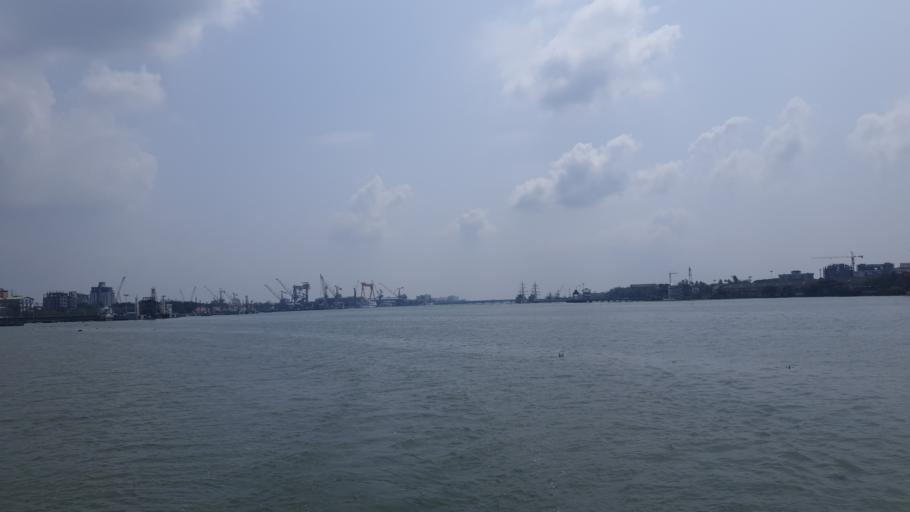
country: IN
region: Kerala
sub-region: Ernakulam
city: Cochin
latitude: 9.9683
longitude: 76.2755
